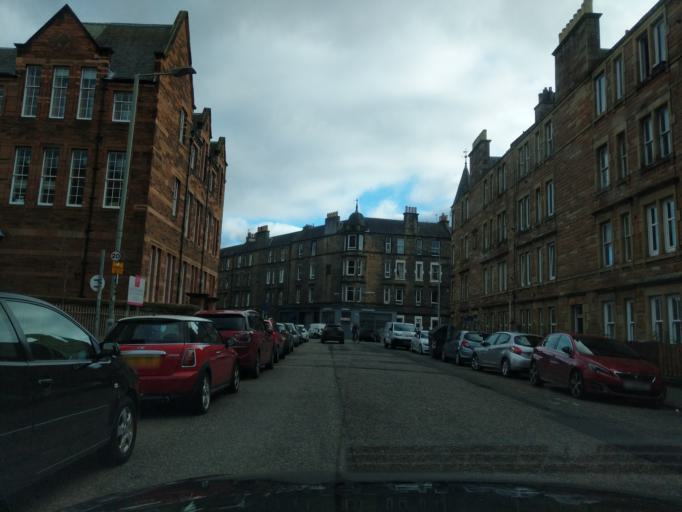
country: GB
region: Scotland
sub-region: West Lothian
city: Seafield
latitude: 55.9617
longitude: -3.1676
